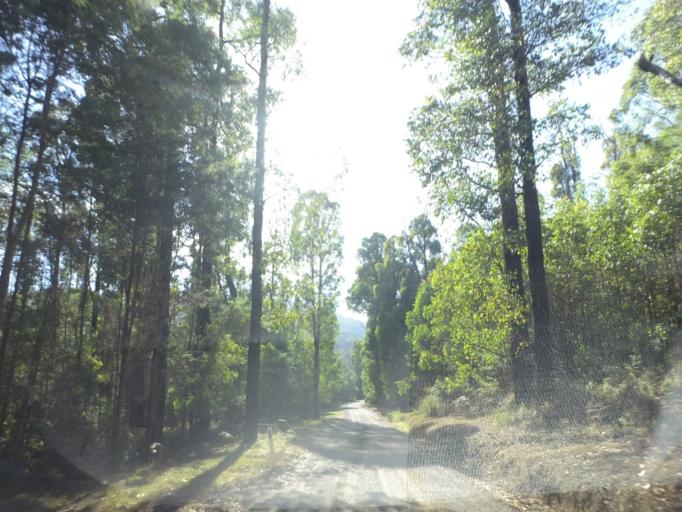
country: AU
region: Victoria
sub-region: Yarra Ranges
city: Millgrove
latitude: -37.5026
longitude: 145.7635
